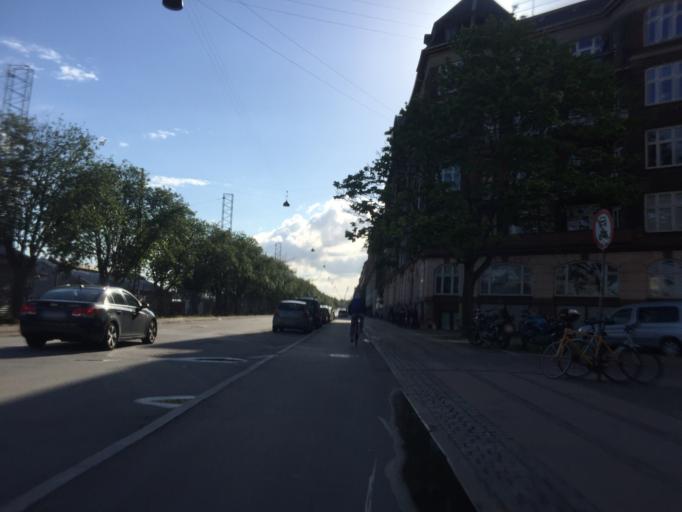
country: DK
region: Capital Region
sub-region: Kobenhavn
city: Copenhagen
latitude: 55.6648
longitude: 12.5538
